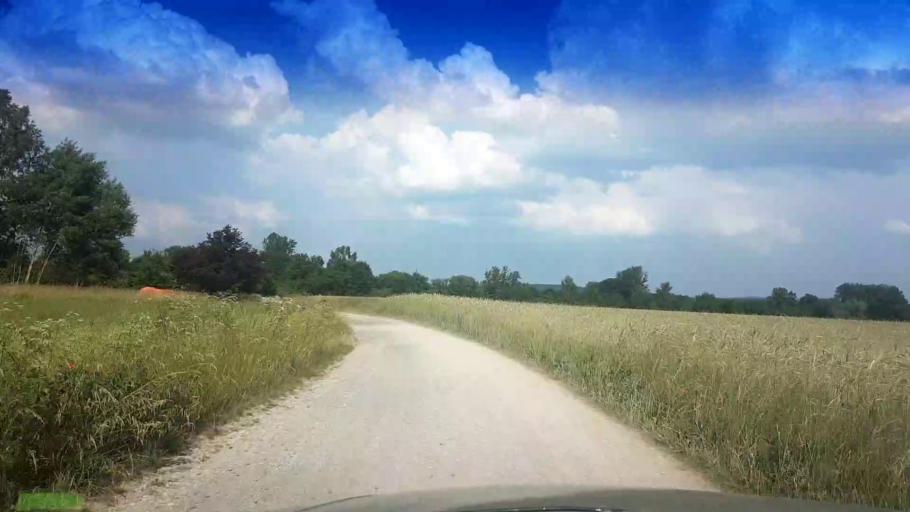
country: DE
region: Bavaria
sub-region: Upper Franconia
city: Kemmern
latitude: 49.9514
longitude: 10.8650
